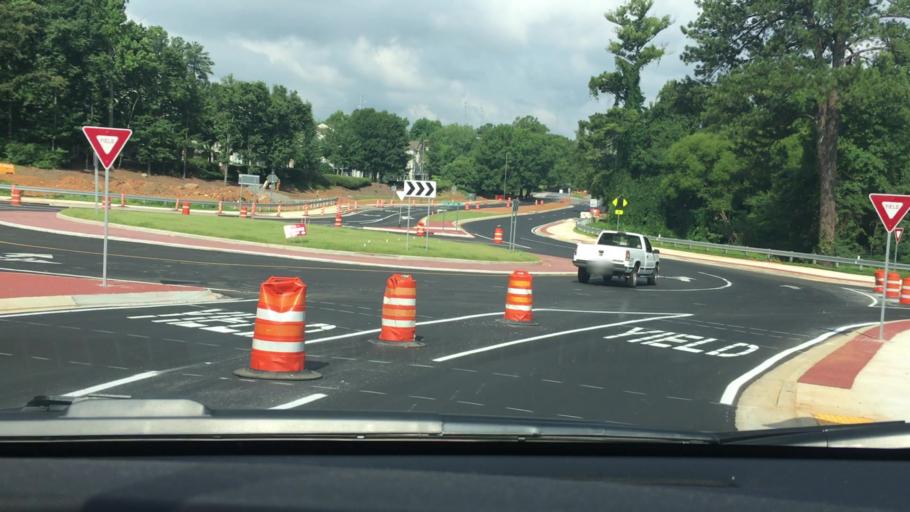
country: US
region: Georgia
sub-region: Cobb County
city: Kennesaw
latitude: 34.0033
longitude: -84.5724
